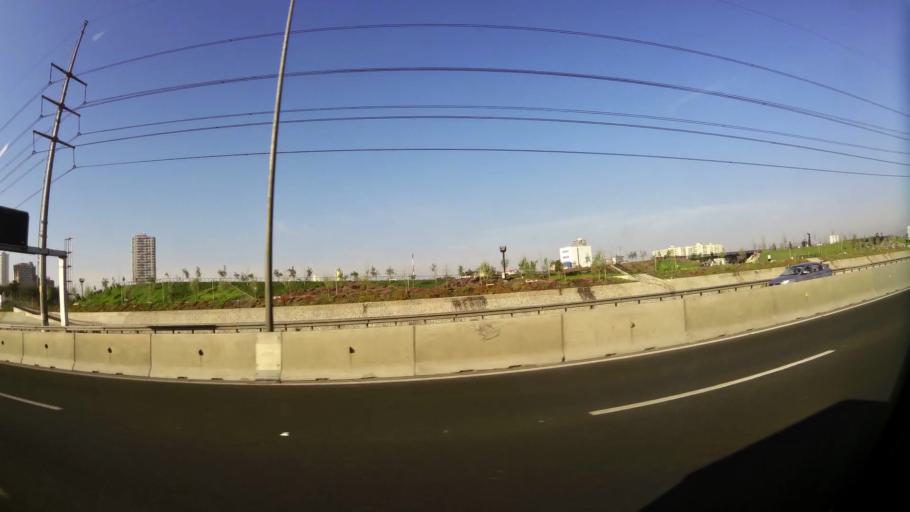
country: CL
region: Santiago Metropolitan
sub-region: Provincia de Santiago
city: Santiago
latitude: -33.4234
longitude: -70.6779
